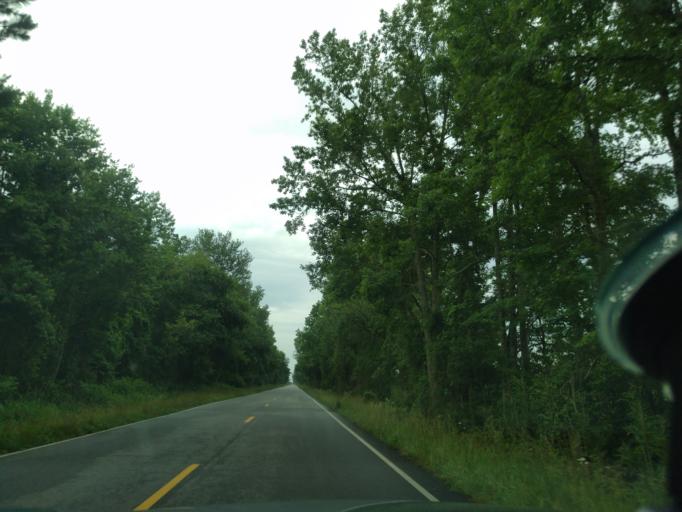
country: US
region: North Carolina
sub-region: Washington County
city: Plymouth
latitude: 35.8570
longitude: -76.5729
